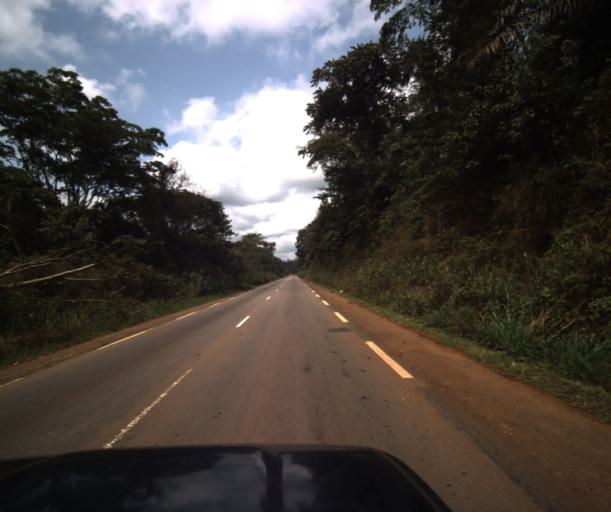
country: CM
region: Centre
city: Mbankomo
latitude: 3.7925
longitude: 11.3268
